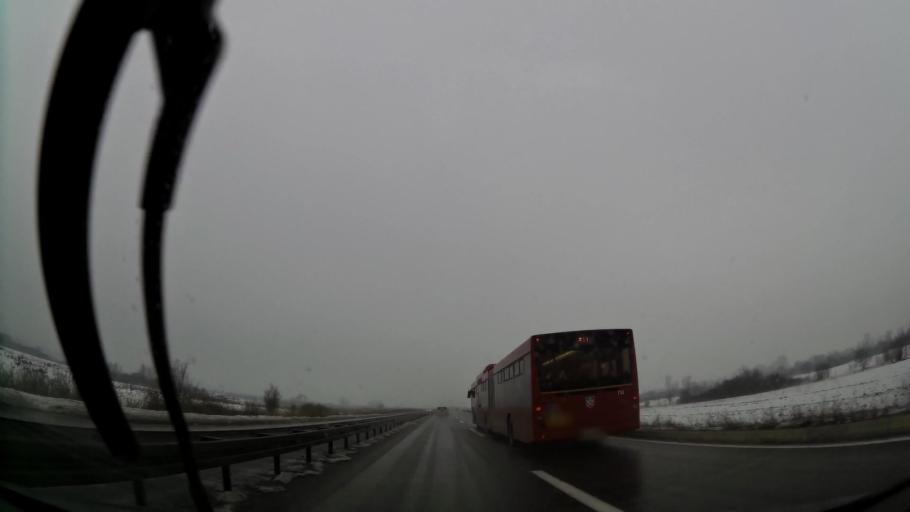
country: RS
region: Central Serbia
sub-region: Belgrade
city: Cukarica
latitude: 44.7498
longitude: 20.3753
